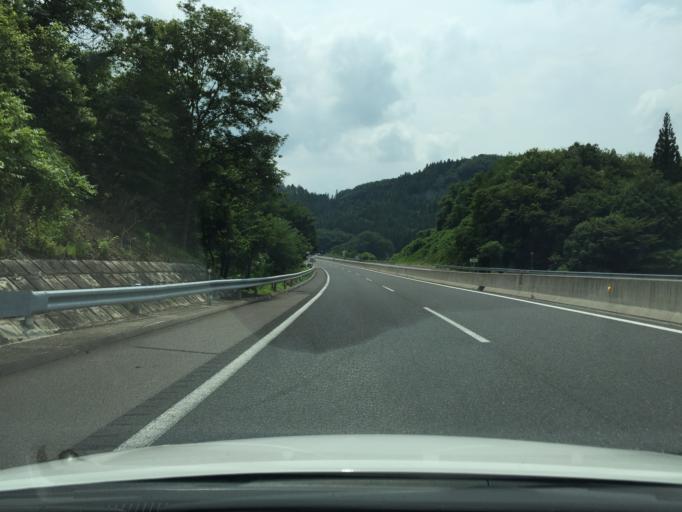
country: JP
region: Fukushima
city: Funehikimachi-funehiki
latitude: 37.3166
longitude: 140.6113
